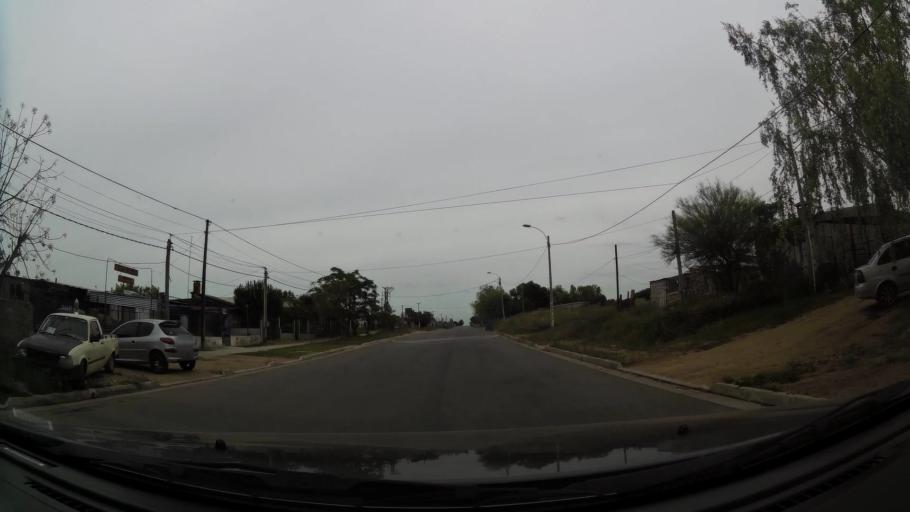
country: UY
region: Canelones
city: La Paz
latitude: -34.7462
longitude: -56.2154
